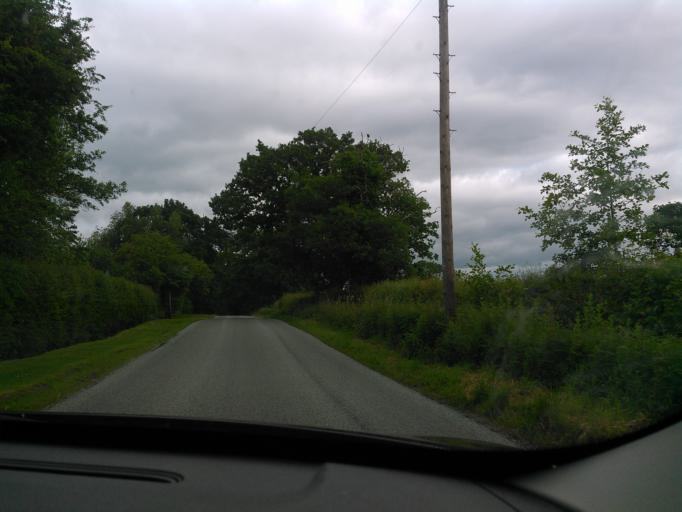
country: GB
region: England
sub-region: Shropshire
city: Wem
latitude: 52.8871
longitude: -2.7511
